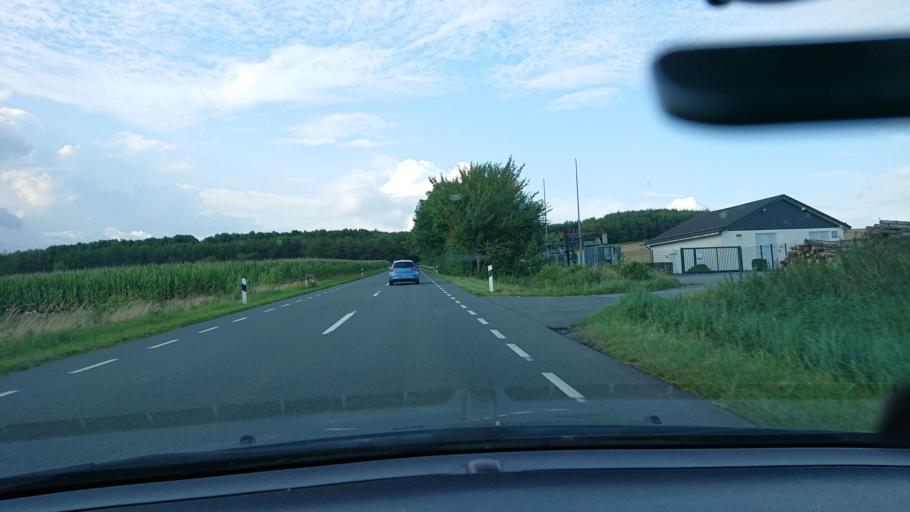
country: DE
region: North Rhine-Westphalia
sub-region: Regierungsbezirk Arnsberg
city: Mohnesee
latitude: 51.5002
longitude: 8.0600
